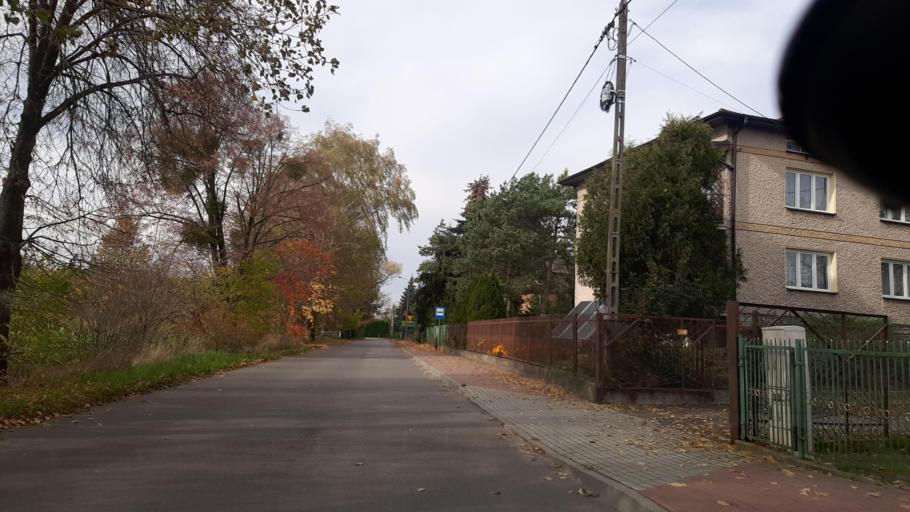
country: PL
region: Lublin Voivodeship
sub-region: Powiat pulawski
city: Markuszow
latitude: 51.3590
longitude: 22.2813
